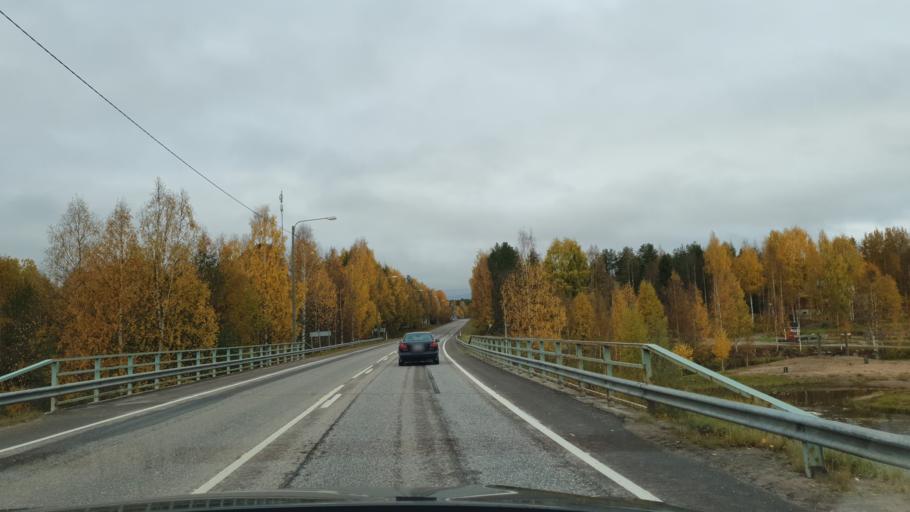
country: FI
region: Lapland
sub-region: Rovaniemi
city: Rovaniemi
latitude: 66.6450
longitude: 25.4662
